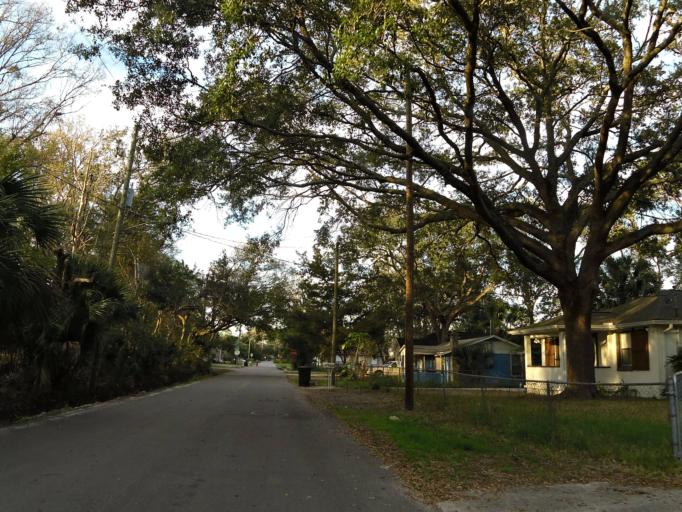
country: US
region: Florida
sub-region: Duval County
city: Jacksonville
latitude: 30.2889
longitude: -81.6423
